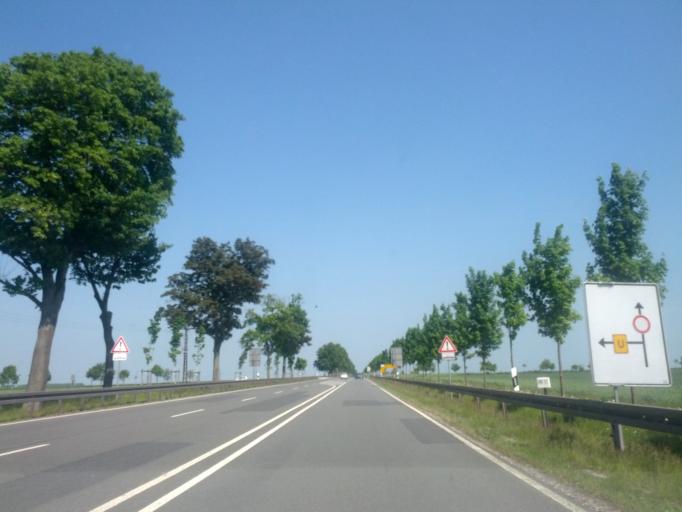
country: DE
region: Thuringia
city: Grabsleben
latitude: 50.9463
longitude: 10.8354
